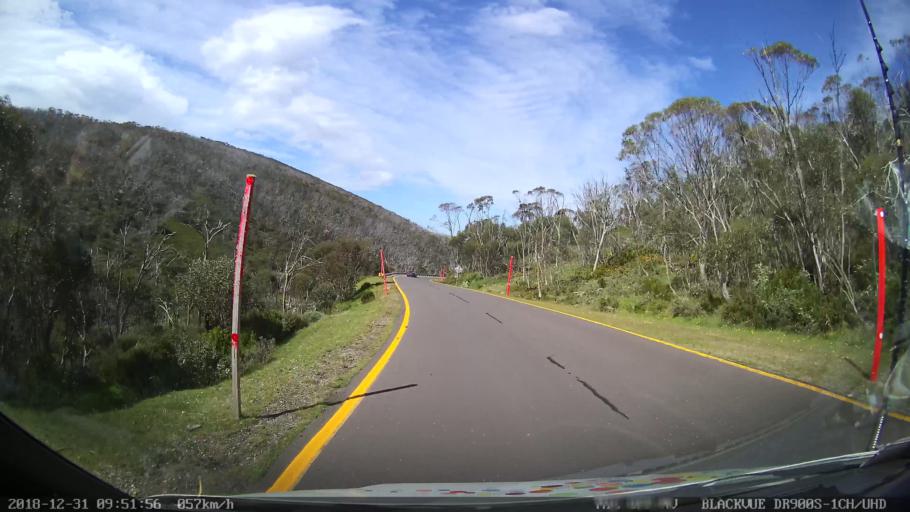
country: AU
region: New South Wales
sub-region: Snowy River
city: Jindabyne
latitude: -36.5247
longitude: 148.2580
